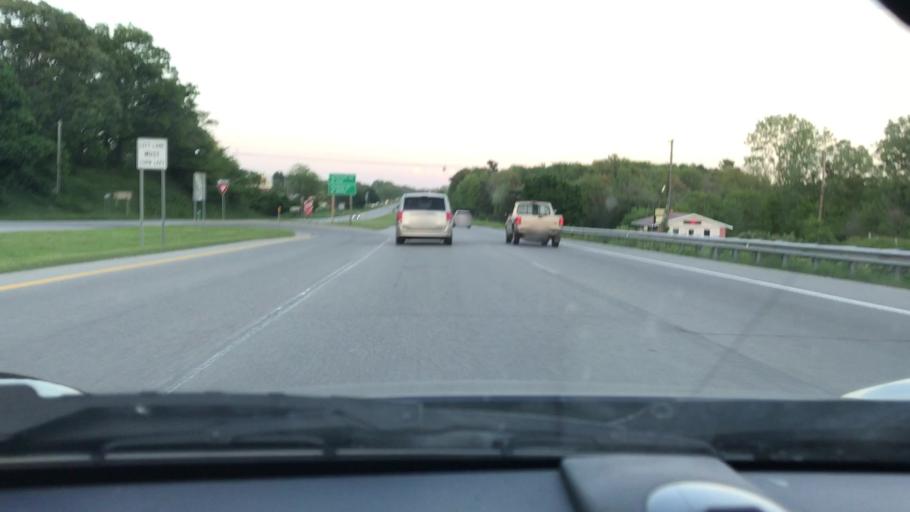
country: US
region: Michigan
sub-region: Muskegon County
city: Muskegon Heights
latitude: 43.1893
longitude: -86.2490
